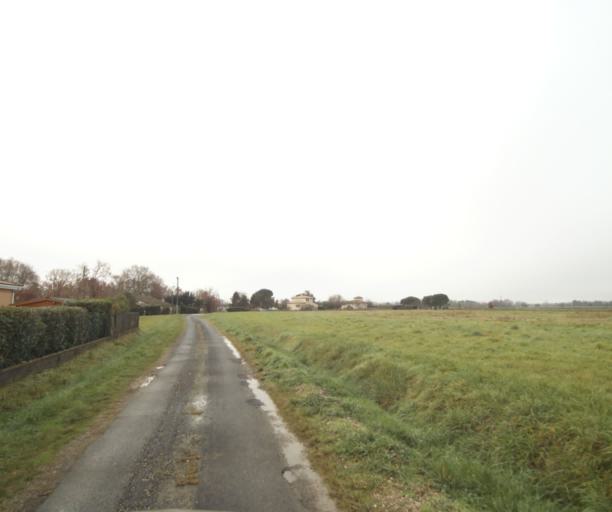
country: FR
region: Midi-Pyrenees
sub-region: Departement de la Haute-Garonne
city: Villemur-sur-Tarn
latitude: 43.8588
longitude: 1.4751
